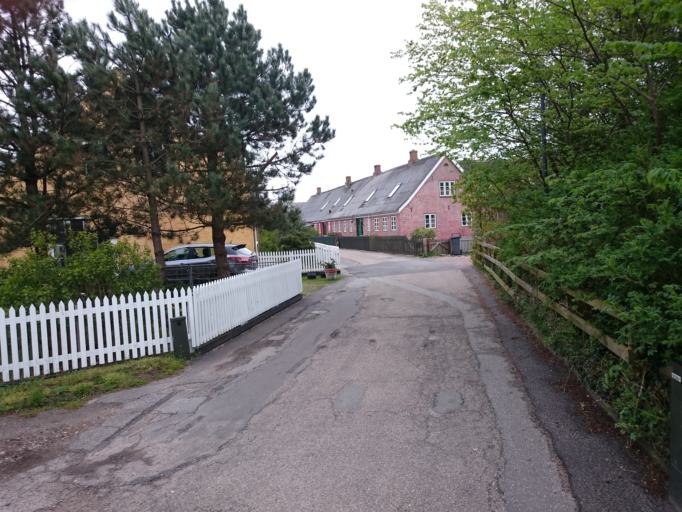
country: DK
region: South Denmark
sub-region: Fano Kommune
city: Nordby
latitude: 55.4488
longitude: 8.4035
